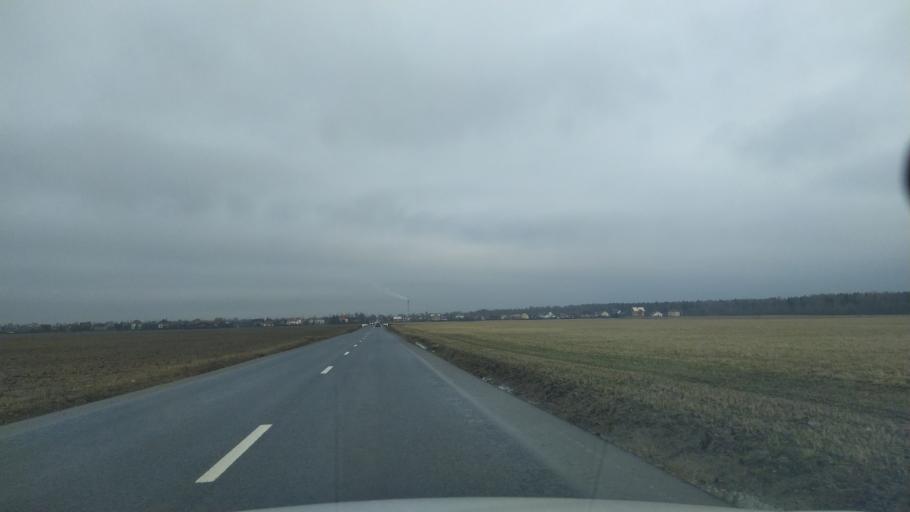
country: RU
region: St.-Petersburg
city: Aleksandrovskaya
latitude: 59.7159
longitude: 30.3367
